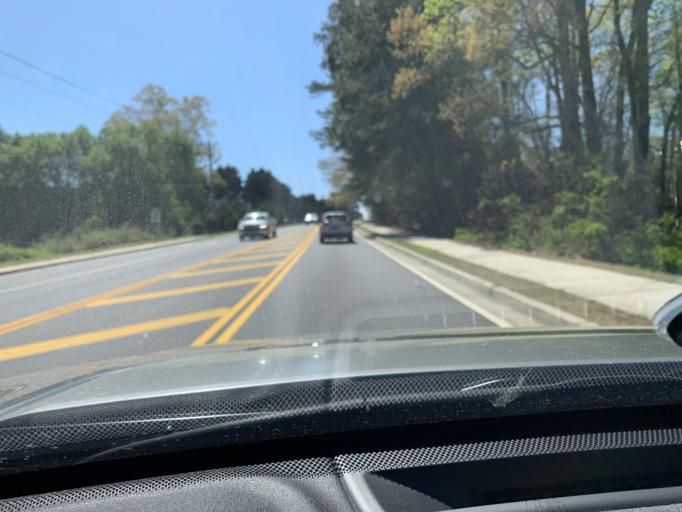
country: US
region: Georgia
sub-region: Fulton County
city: Milton
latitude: 34.1752
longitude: -84.2244
